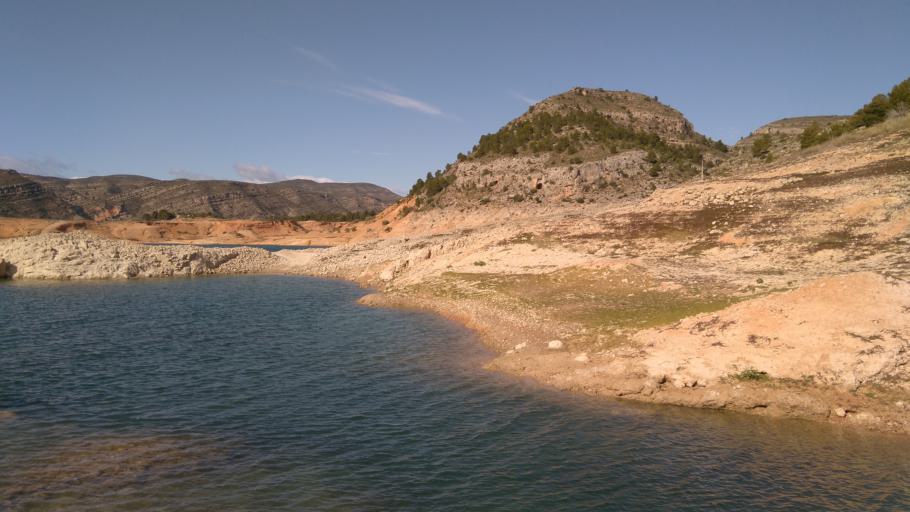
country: ES
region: Valencia
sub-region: Provincia de Valencia
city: Sumacarcer
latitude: 39.1548
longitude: -0.6585
